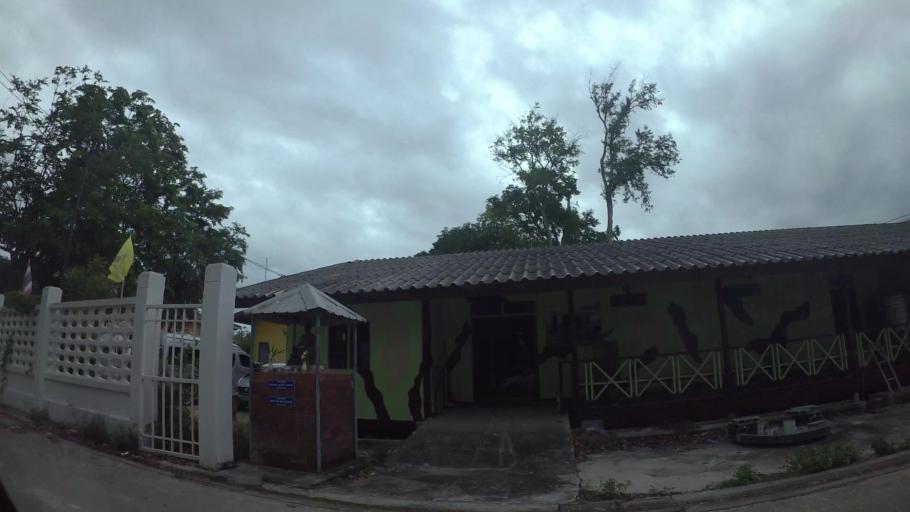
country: TH
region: Rayong
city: Rayong
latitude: 12.6685
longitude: 101.2756
